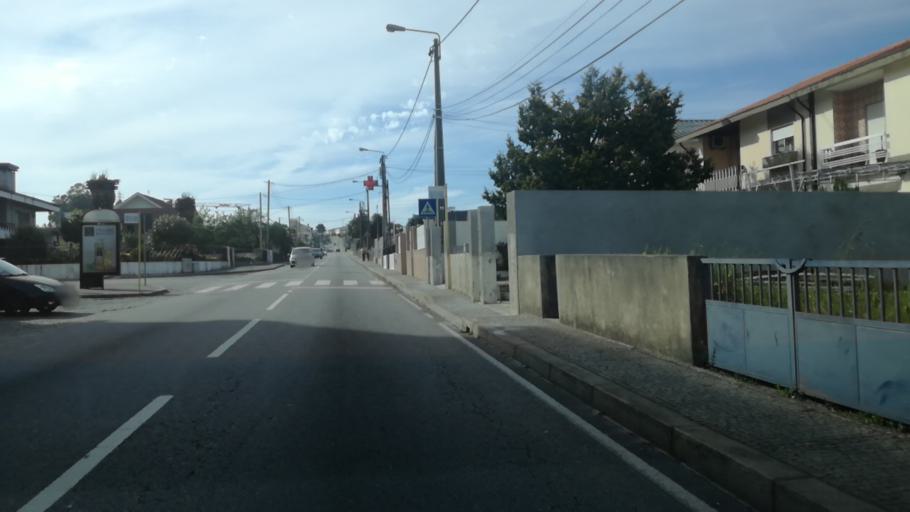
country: PT
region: Porto
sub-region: Valongo
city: Ermesinde
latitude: 41.2279
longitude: -8.5680
